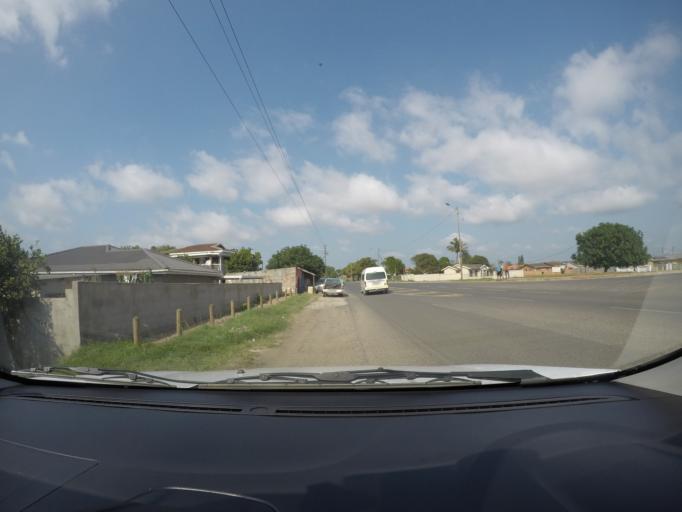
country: ZA
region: KwaZulu-Natal
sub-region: uThungulu District Municipality
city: eSikhawini
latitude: -28.8723
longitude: 31.9206
